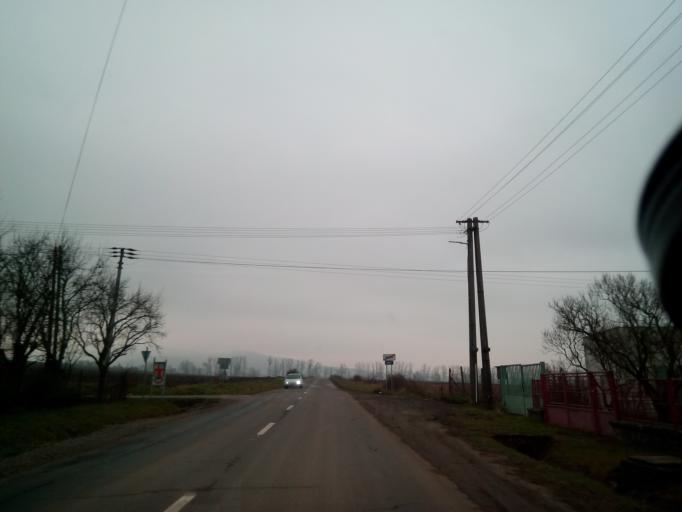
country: SK
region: Kosicky
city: Kosice
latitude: 48.7059
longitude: 21.4376
